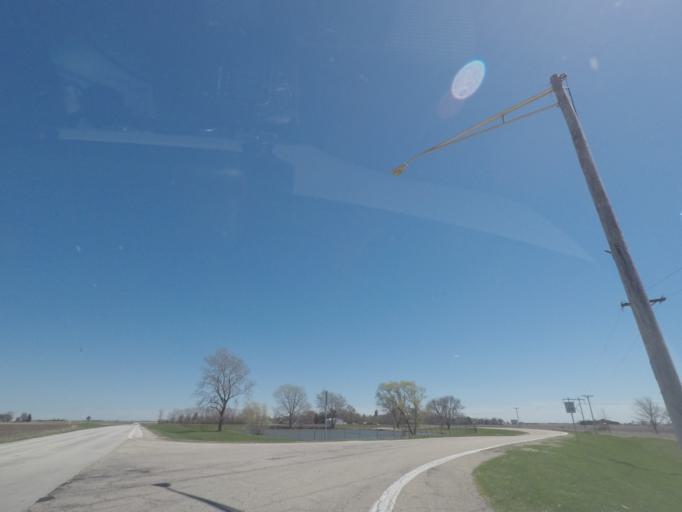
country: US
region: Illinois
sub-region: Logan County
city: Mount Pulaski
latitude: 39.9707
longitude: -89.1740
